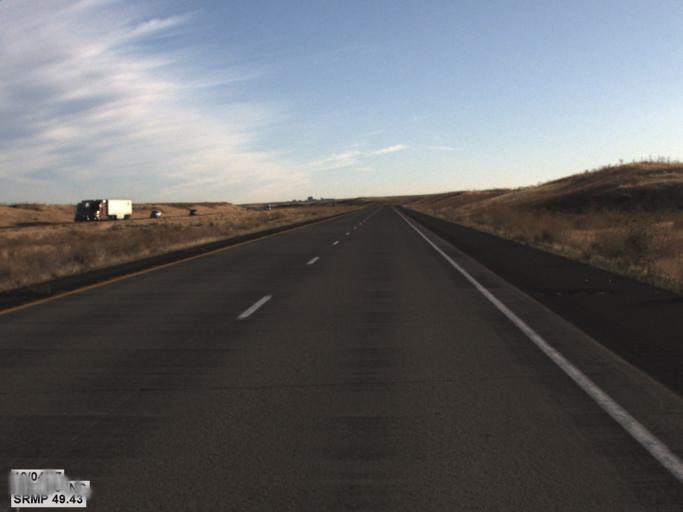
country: US
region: Washington
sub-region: Franklin County
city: Connell
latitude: 46.5988
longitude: -118.9363
